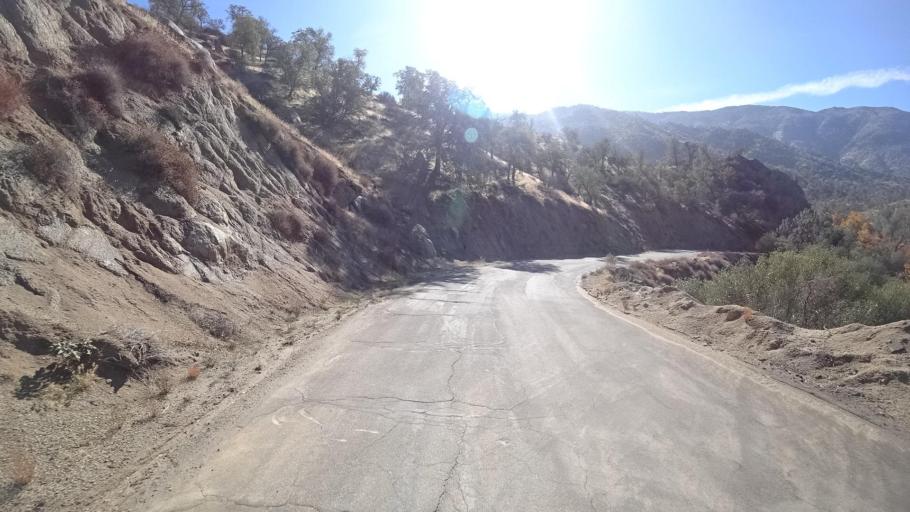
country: US
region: California
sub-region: Kern County
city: Bodfish
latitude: 35.5368
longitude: -118.6146
